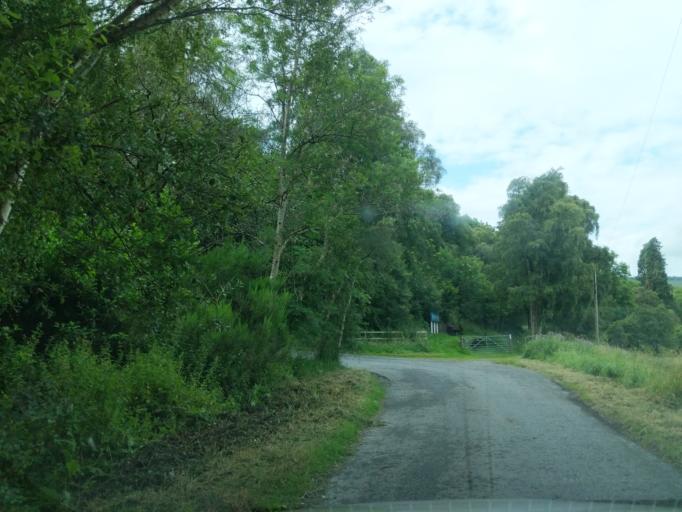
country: GB
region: Scotland
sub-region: Moray
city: Rothes
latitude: 57.4560
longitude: -3.2731
